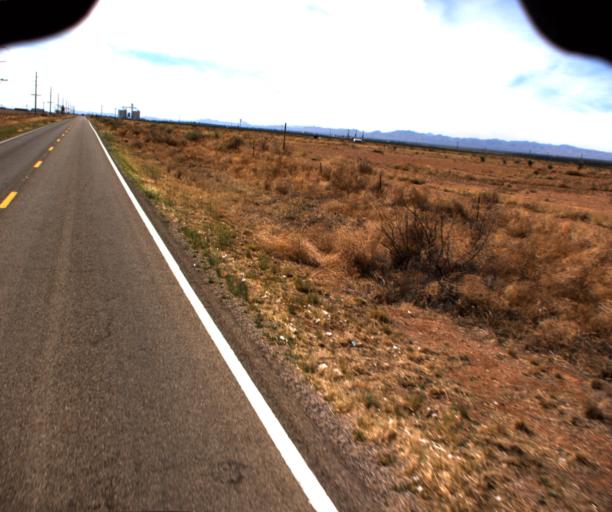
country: US
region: Arizona
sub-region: Cochise County
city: Tombstone
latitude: 31.7706
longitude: -109.6906
